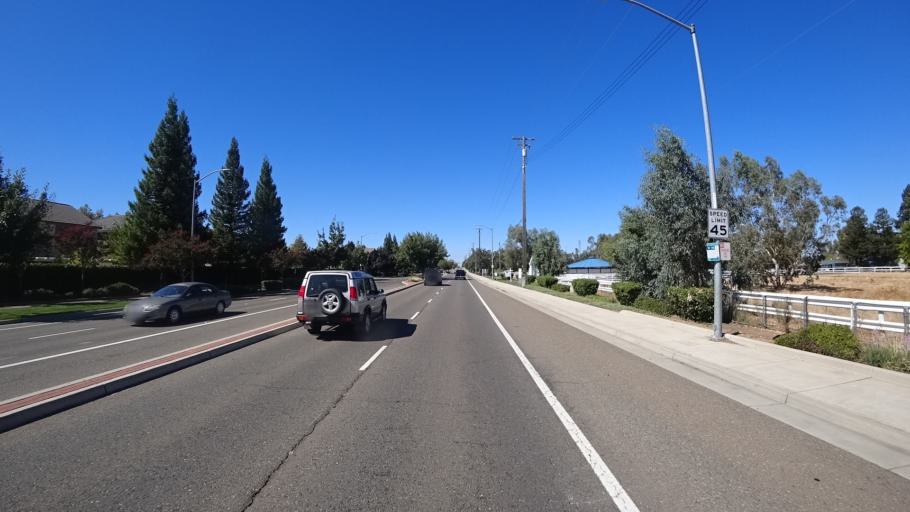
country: US
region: California
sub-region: Sacramento County
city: Elk Grove
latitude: 38.4238
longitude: -121.3446
